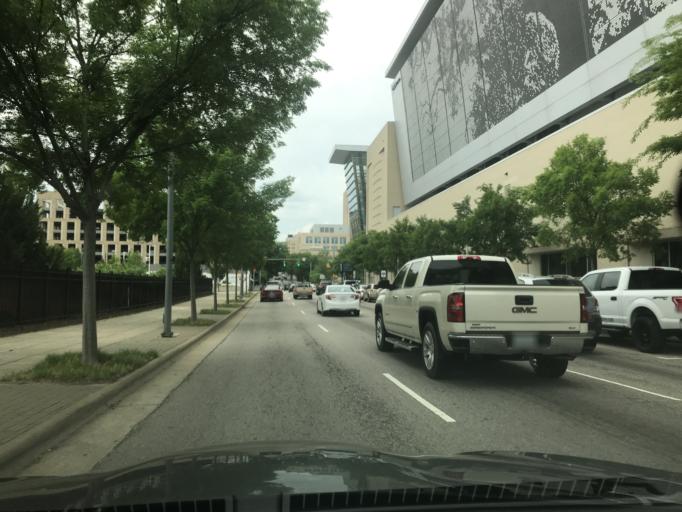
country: US
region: North Carolina
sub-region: Wake County
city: Raleigh
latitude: 35.7733
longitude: -78.6421
